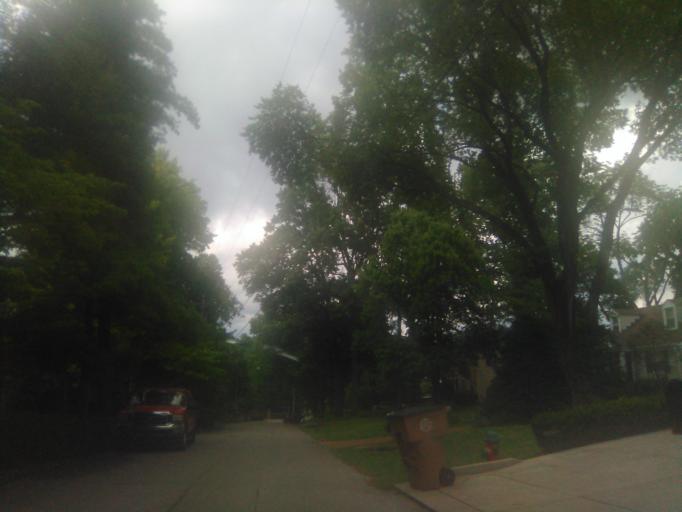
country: US
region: Tennessee
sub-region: Davidson County
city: Belle Meade
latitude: 36.1121
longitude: -86.8397
